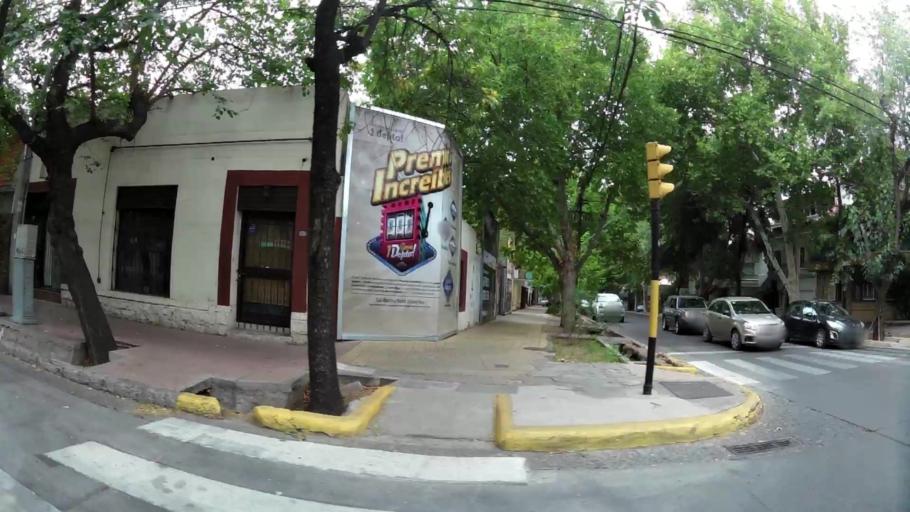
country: AR
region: Mendoza
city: Mendoza
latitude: -32.8892
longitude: -68.8590
